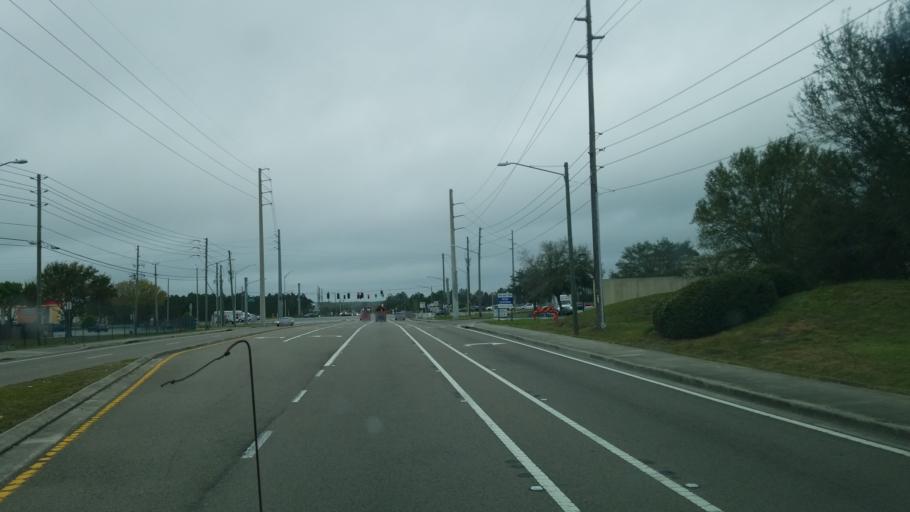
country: US
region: Florida
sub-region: Lake County
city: Four Corners
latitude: 28.2546
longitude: -81.6564
